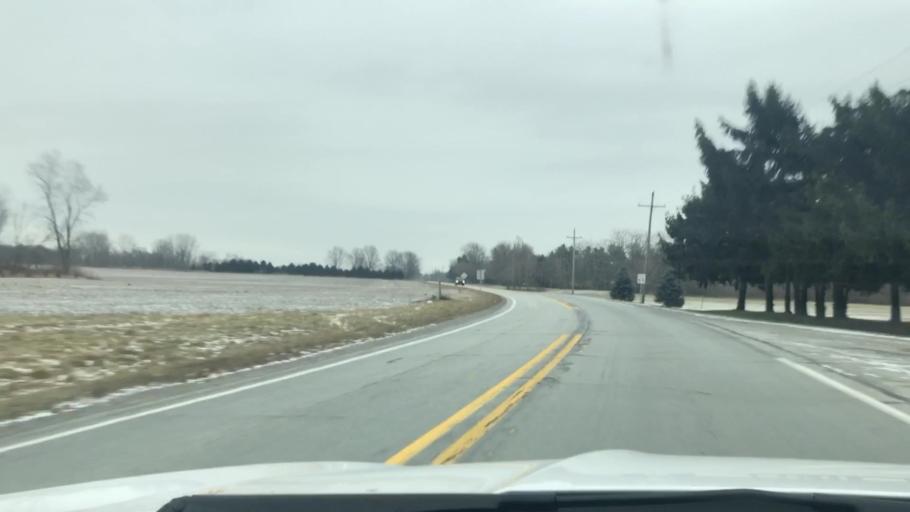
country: US
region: Indiana
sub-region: Fulton County
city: Rochester
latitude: 41.0578
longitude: -86.1683
